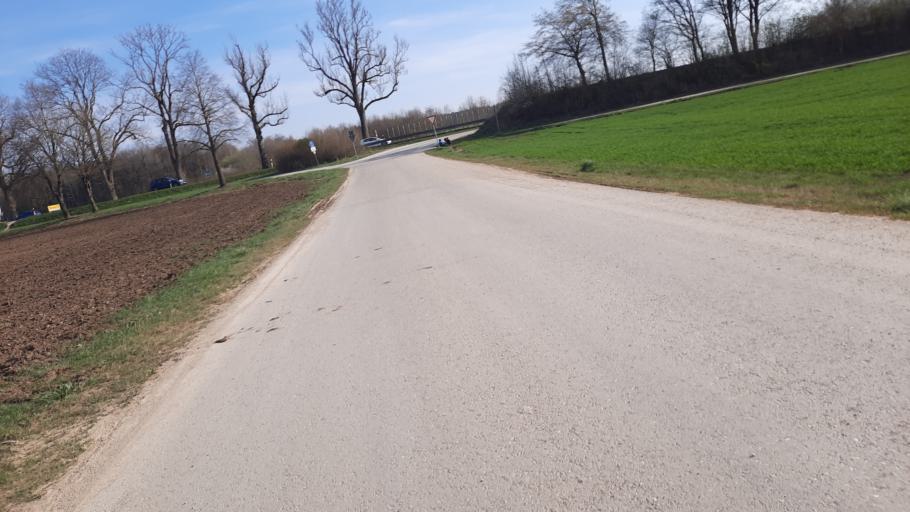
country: DE
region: Bavaria
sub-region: Upper Bavaria
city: Zorneding
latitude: 48.0839
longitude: 11.8444
